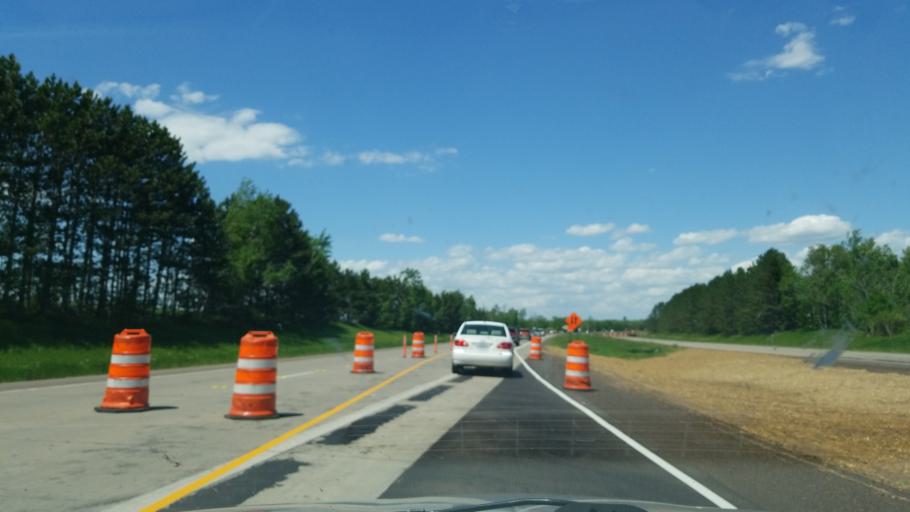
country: US
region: Minnesota
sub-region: Pine County
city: Sandstone
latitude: 46.2689
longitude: -92.8253
